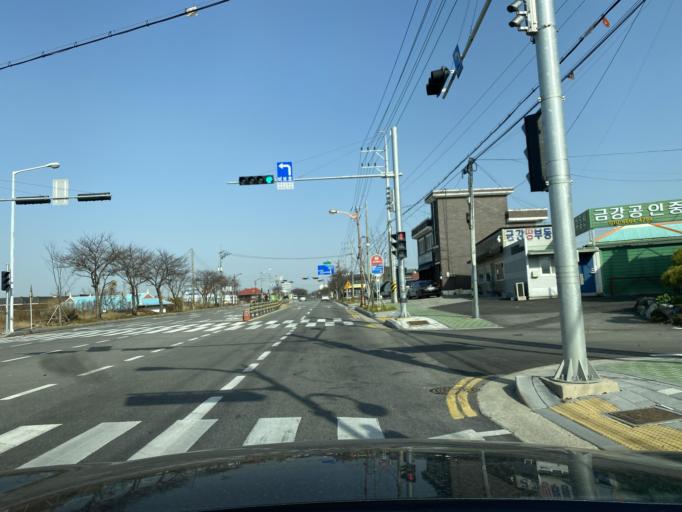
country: KR
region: Chungcheongnam-do
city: Yesan
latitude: 36.7066
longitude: 126.8396
